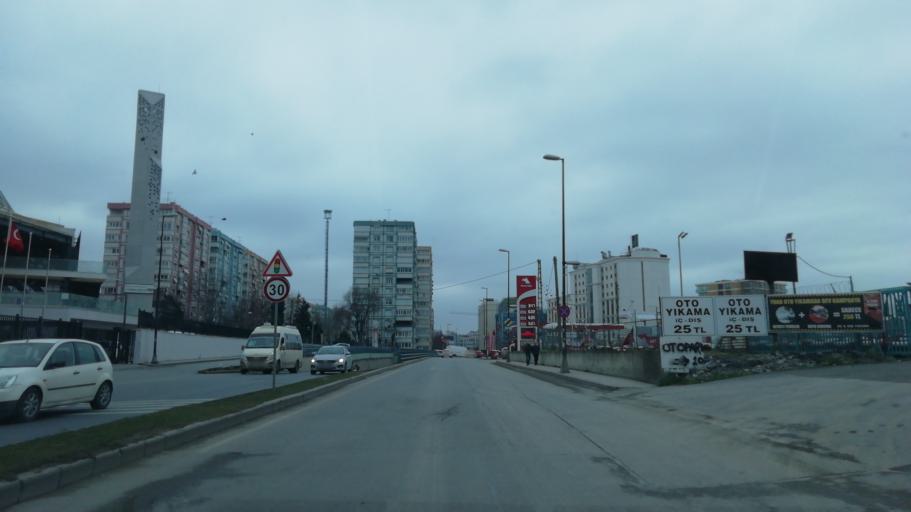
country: TR
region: Istanbul
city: Mahmutbey
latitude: 41.0129
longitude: 28.8181
